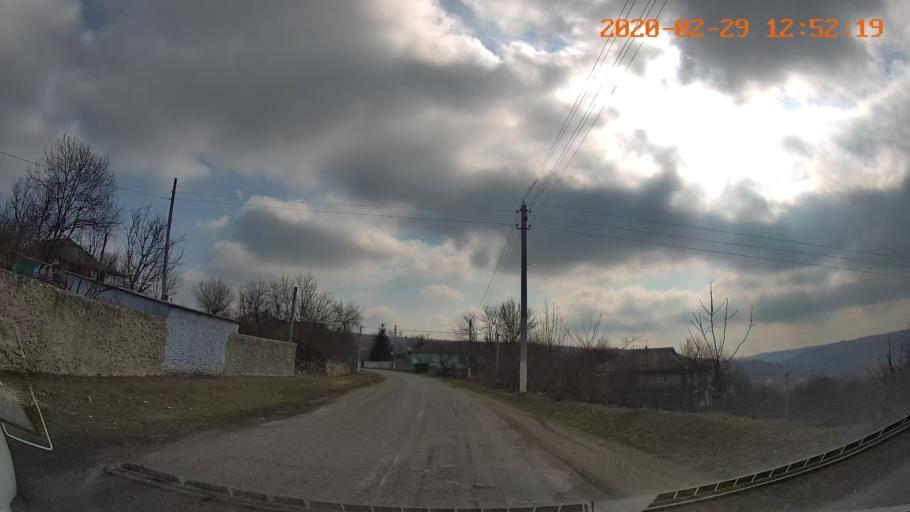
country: MD
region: Telenesti
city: Camenca
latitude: 48.1123
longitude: 28.7328
